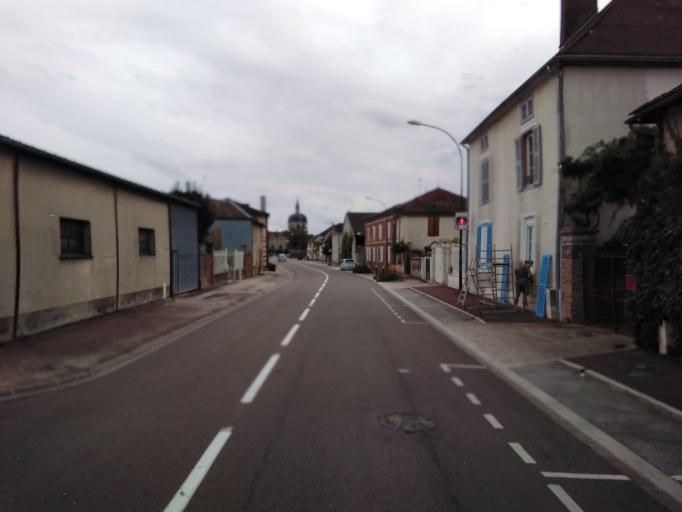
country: FR
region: Champagne-Ardenne
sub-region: Departement de l'Aube
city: Brienne-le-Chateau
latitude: 48.3524
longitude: 4.5331
